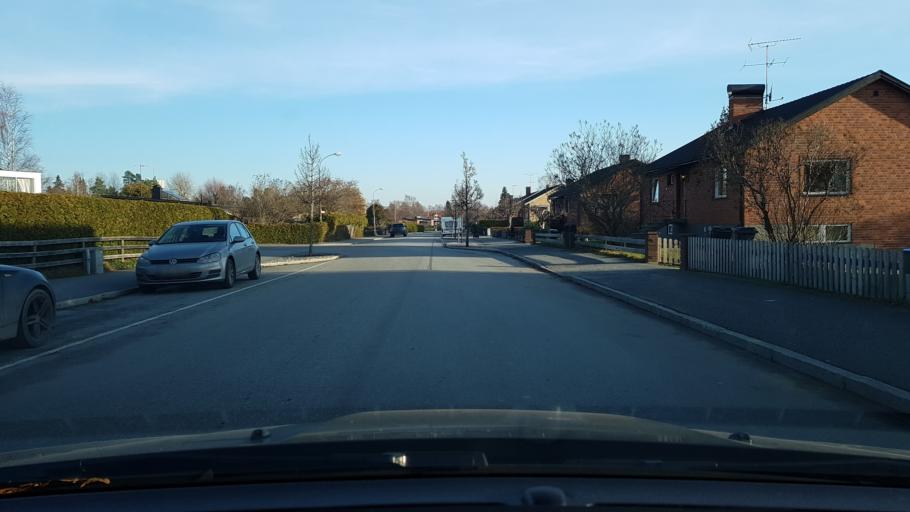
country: SE
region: Stockholm
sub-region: Norrtalje Kommun
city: Rimbo
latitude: 59.7404
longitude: 18.3464
